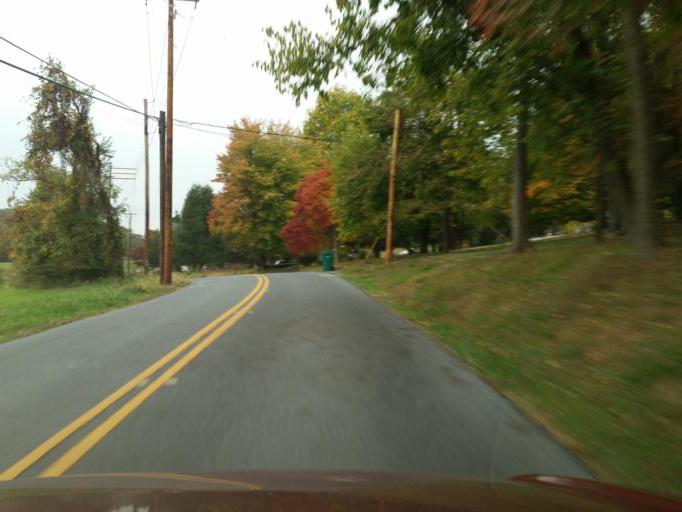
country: US
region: Pennsylvania
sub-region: Dauphin County
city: Hummelstown
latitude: 40.2340
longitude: -76.6834
